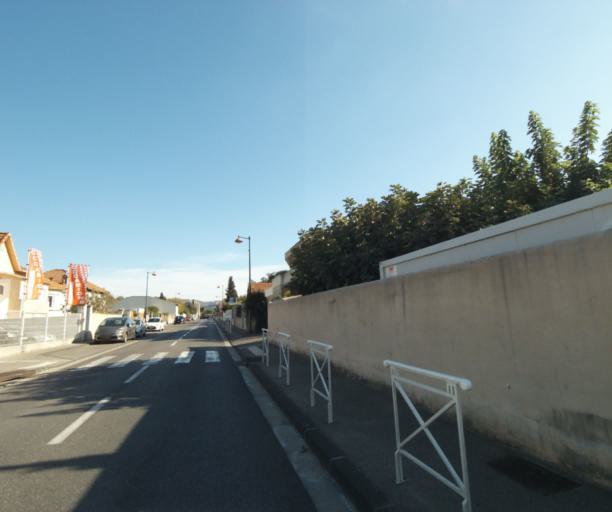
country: FR
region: Provence-Alpes-Cote d'Azur
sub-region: Departement des Bouches-du-Rhone
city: Saint-Victoret
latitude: 43.4121
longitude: 5.2507
